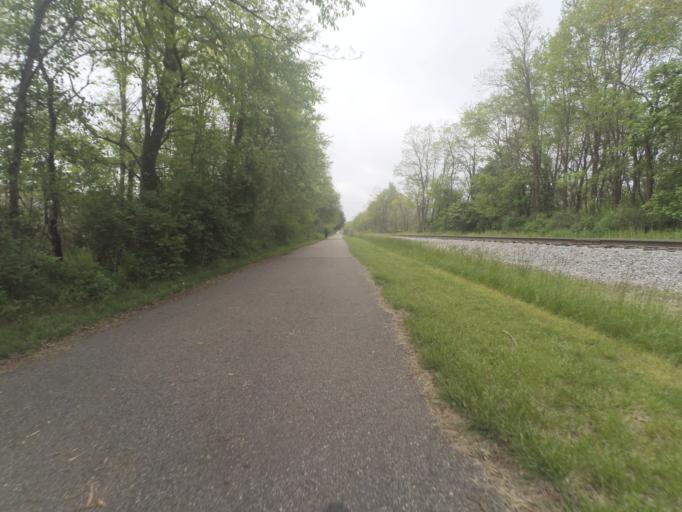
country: US
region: Ohio
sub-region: Portage County
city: Kent
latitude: 41.1665
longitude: -81.3391
